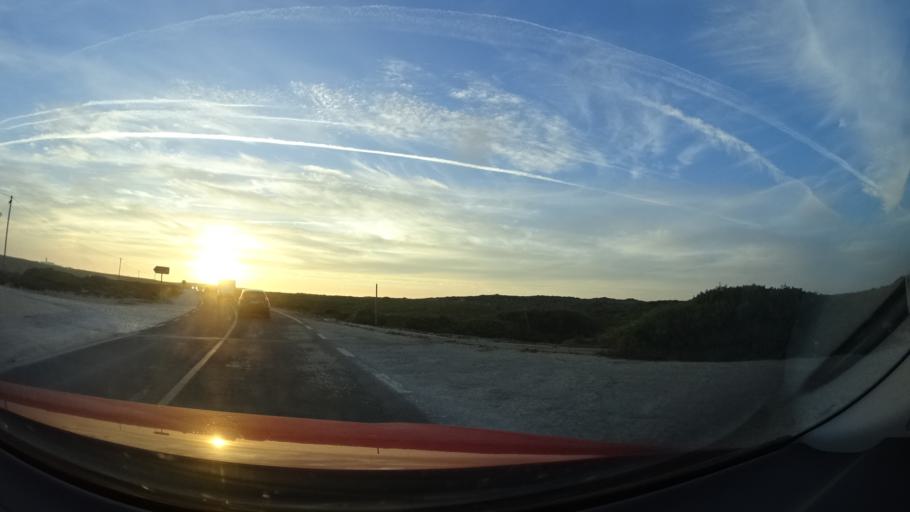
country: PT
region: Faro
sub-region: Vila do Bispo
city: Sagres
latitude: 37.0281
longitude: -8.9812
